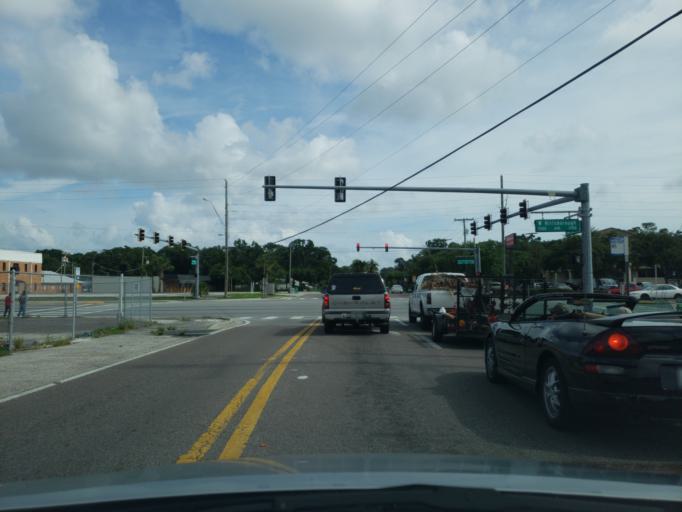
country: US
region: Florida
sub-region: Hillsborough County
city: Egypt Lake-Leto
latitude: 27.9964
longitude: -82.4762
